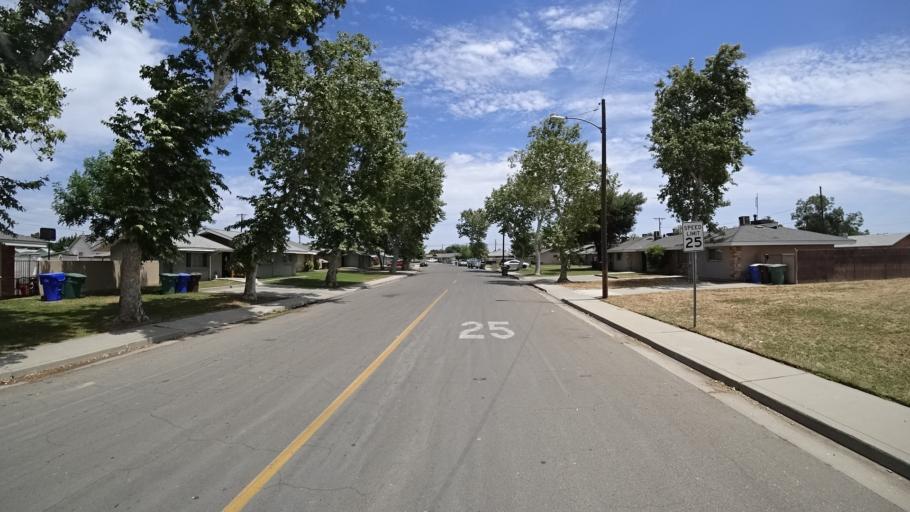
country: US
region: California
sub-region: Kings County
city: Armona
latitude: 36.3115
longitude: -119.7147
